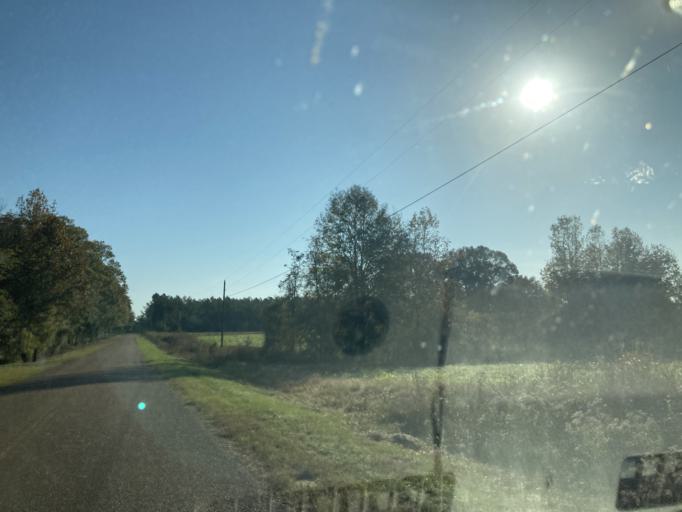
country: US
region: Mississippi
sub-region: Madison County
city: Canton
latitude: 32.7130
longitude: -90.1747
